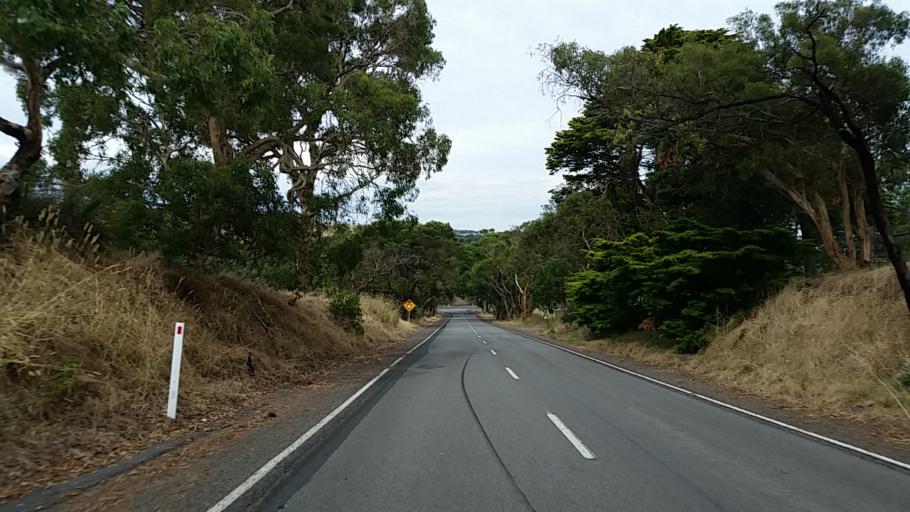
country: AU
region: South Australia
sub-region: Onkaparinga
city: Aldinga
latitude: -35.3771
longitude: 138.4631
